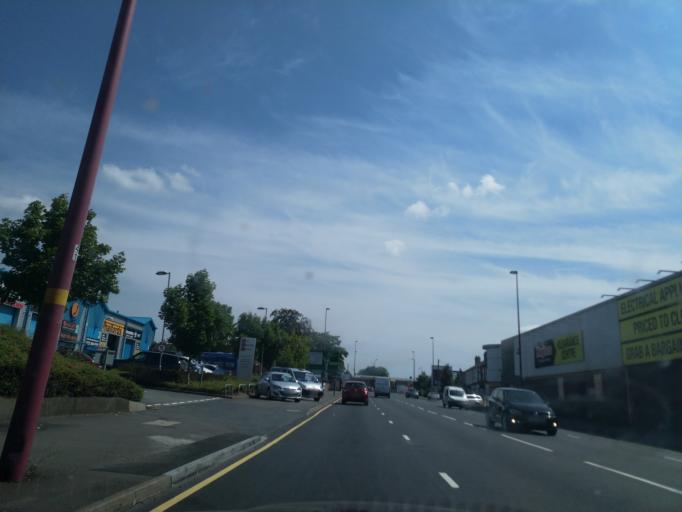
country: GB
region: England
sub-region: Sandwell
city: Smethwick
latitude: 52.5097
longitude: -1.9592
